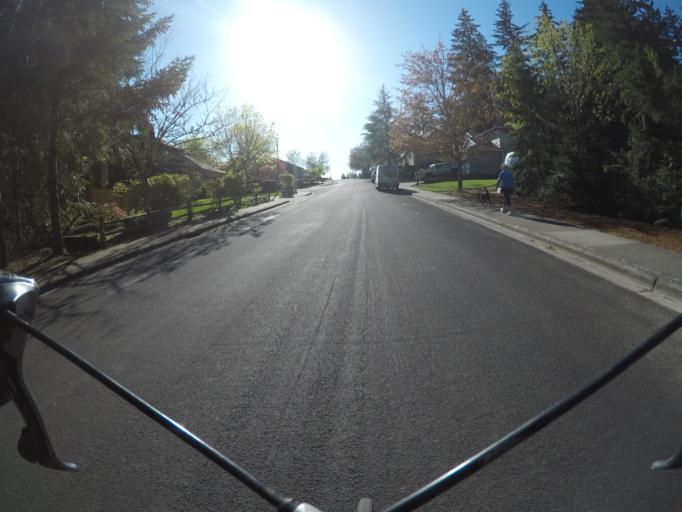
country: US
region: Oregon
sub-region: Washington County
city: King City
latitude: 45.4071
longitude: -122.8294
